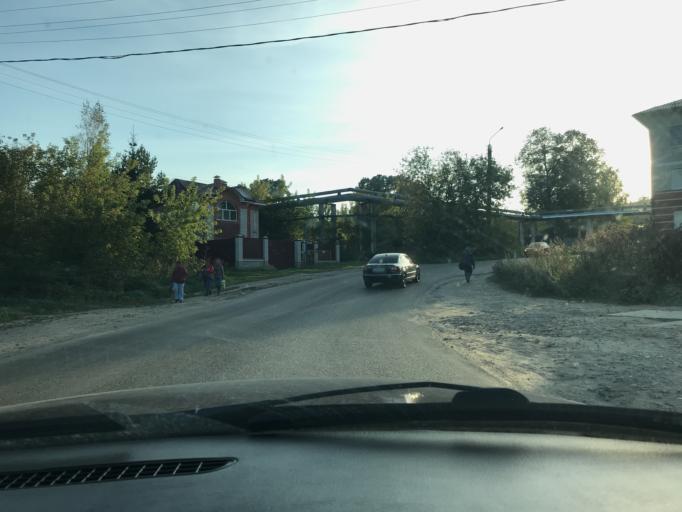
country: RU
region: Kaluga
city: Kondrovo
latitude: 54.7808
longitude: 35.9298
